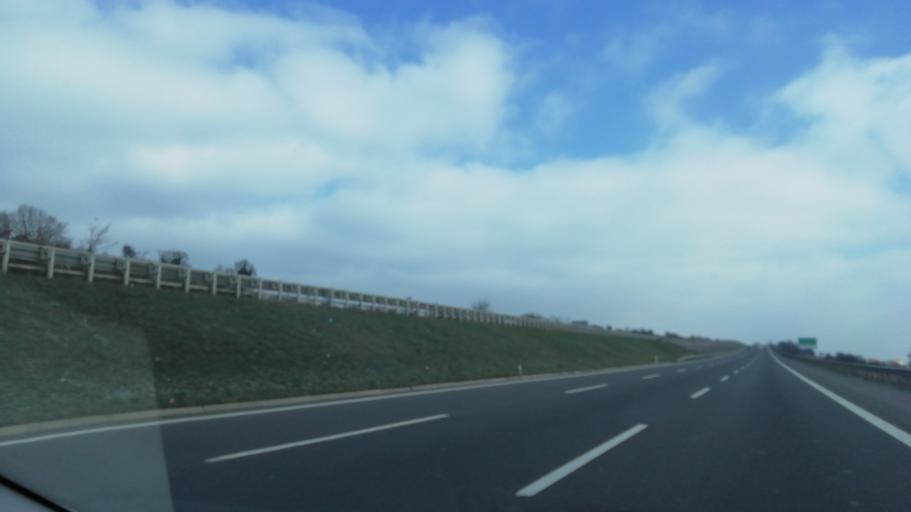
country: TR
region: Bolu
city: Bolu
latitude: 40.7228
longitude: 31.4983
